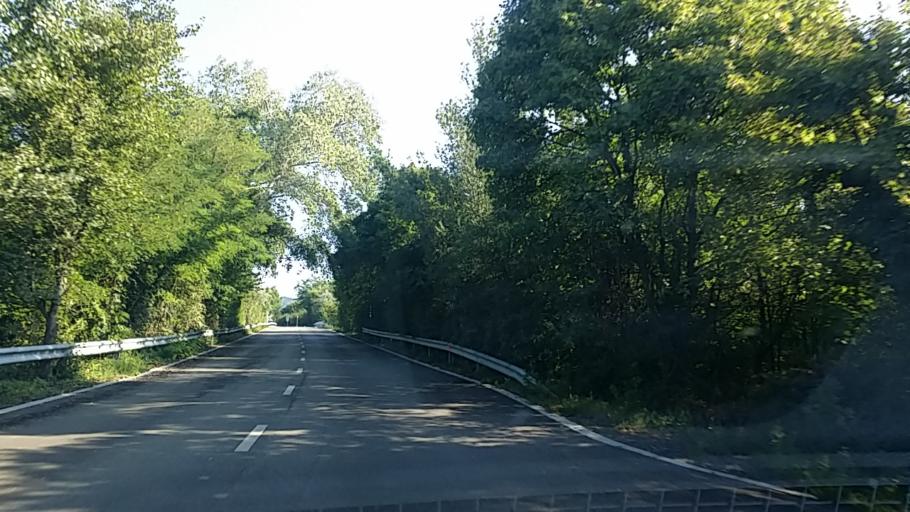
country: HU
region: Komarom-Esztergom
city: Tatabanya
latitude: 47.5754
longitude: 18.4260
